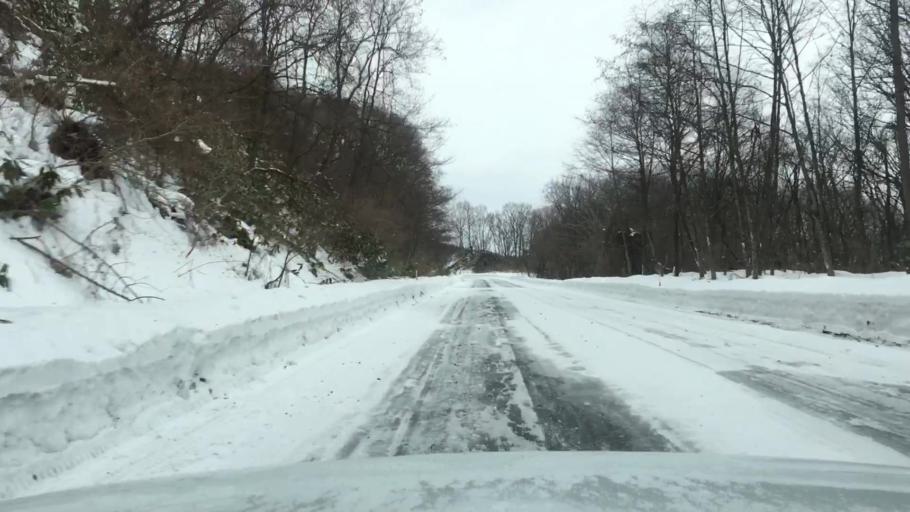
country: JP
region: Iwate
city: Shizukuishi
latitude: 39.9410
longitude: 140.9964
